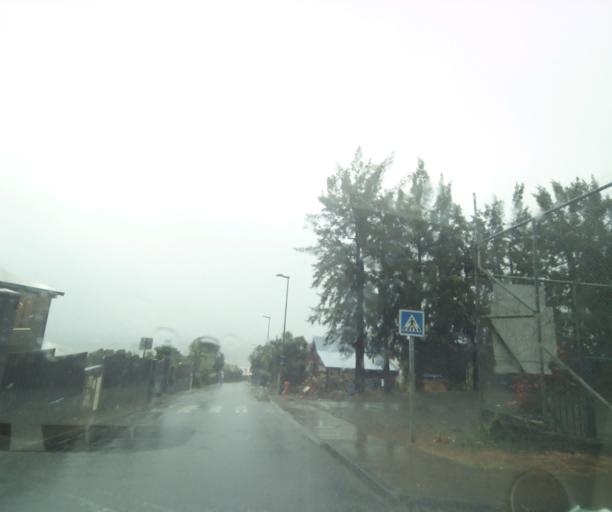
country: RE
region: Reunion
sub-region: Reunion
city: La Possession
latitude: -20.9806
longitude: 55.3388
